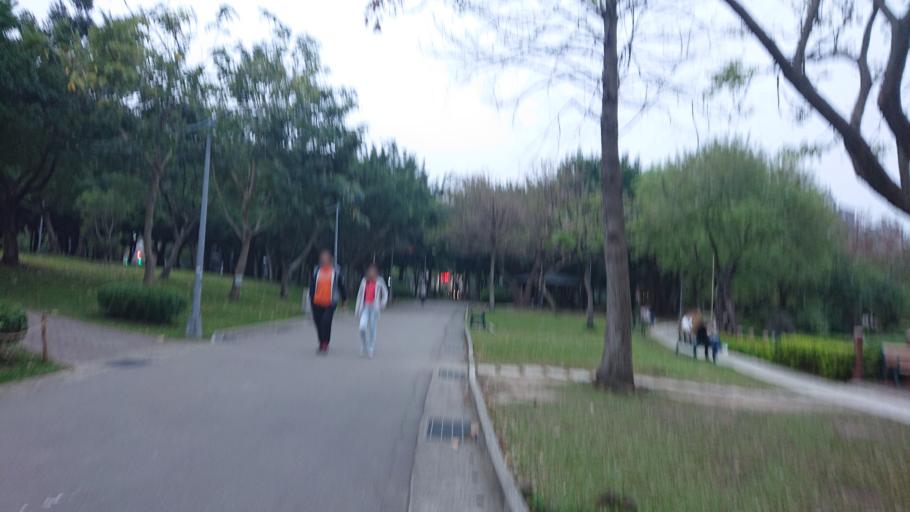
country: TW
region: Taipei
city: Taipei
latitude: 25.0309
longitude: 121.5350
